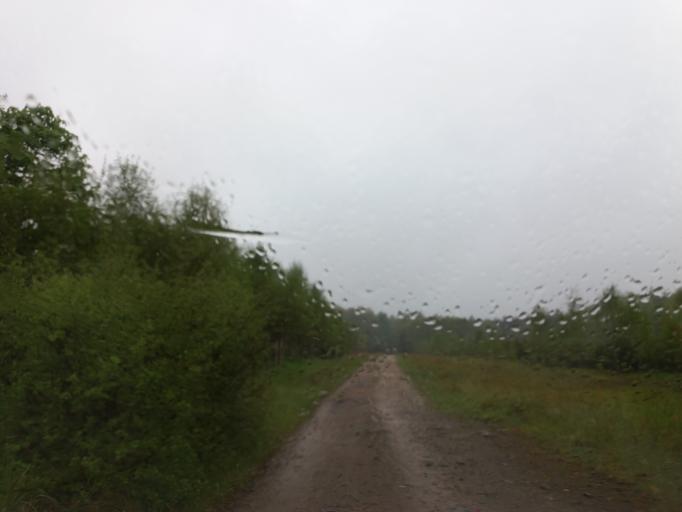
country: PL
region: West Pomeranian Voivodeship
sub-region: Powiat walecki
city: Tuczno
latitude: 53.2289
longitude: 16.0570
